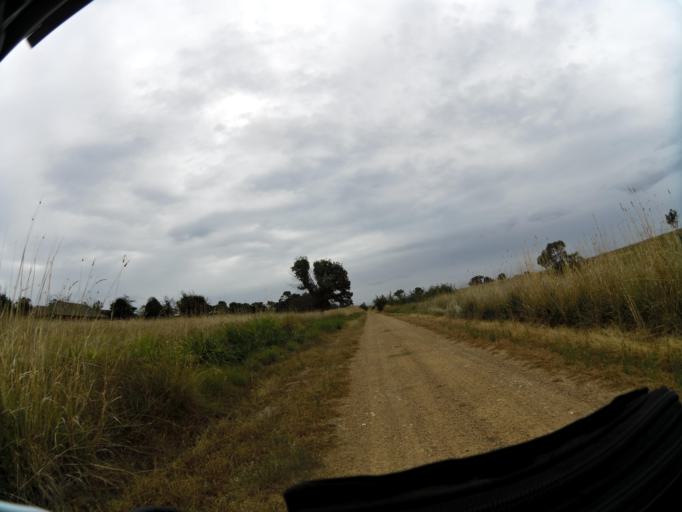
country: AU
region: New South Wales
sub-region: Albury Municipality
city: East Albury
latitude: -36.2072
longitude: 147.0525
